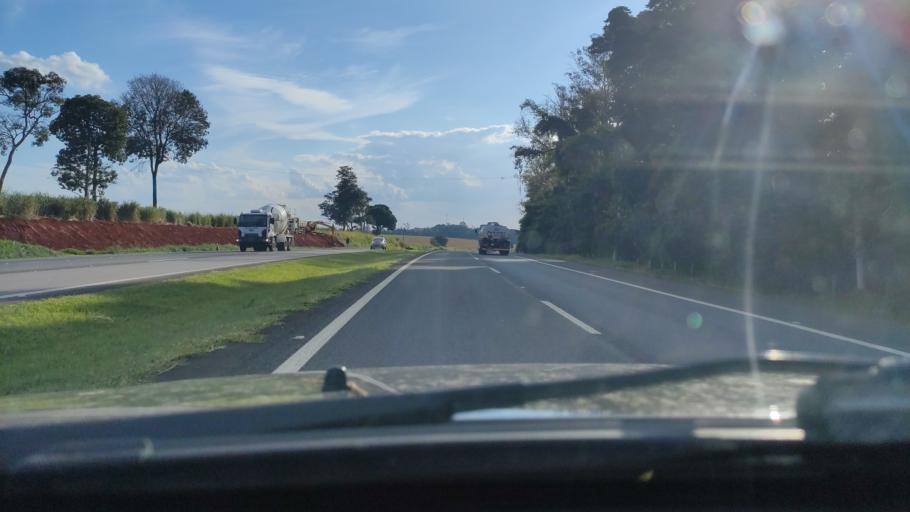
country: BR
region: Sao Paulo
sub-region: Itapira
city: Itapira
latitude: -22.4530
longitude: -46.8576
